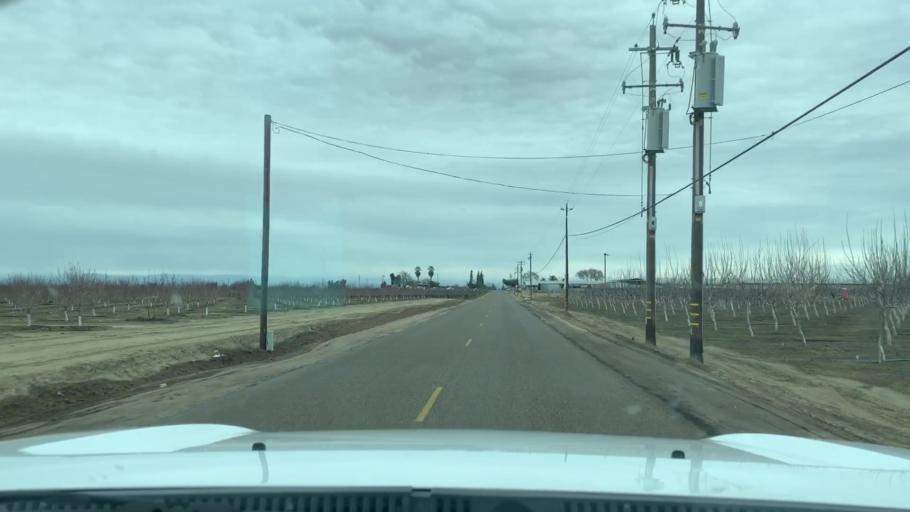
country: US
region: California
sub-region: Fresno County
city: Fowler
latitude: 36.5472
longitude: -119.7070
